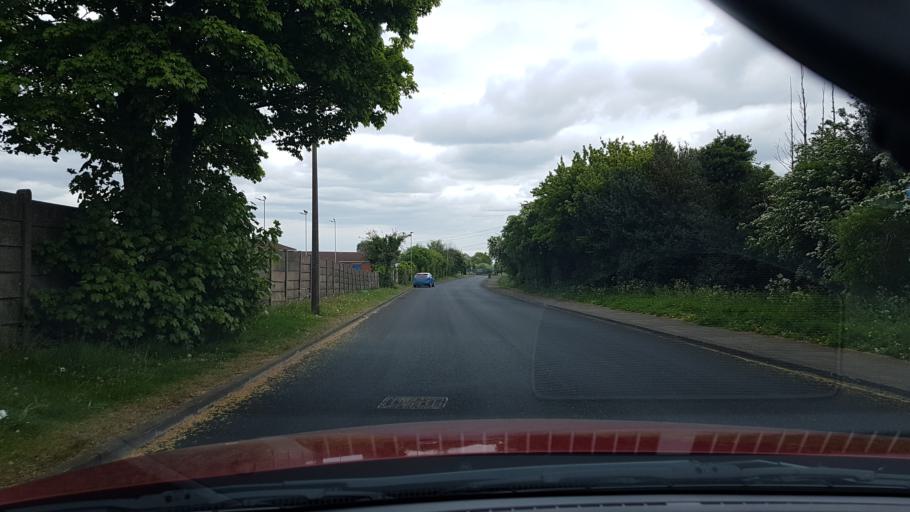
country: GB
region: England
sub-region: Rotherham
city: Maltby
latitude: 53.4165
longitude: -1.1941
